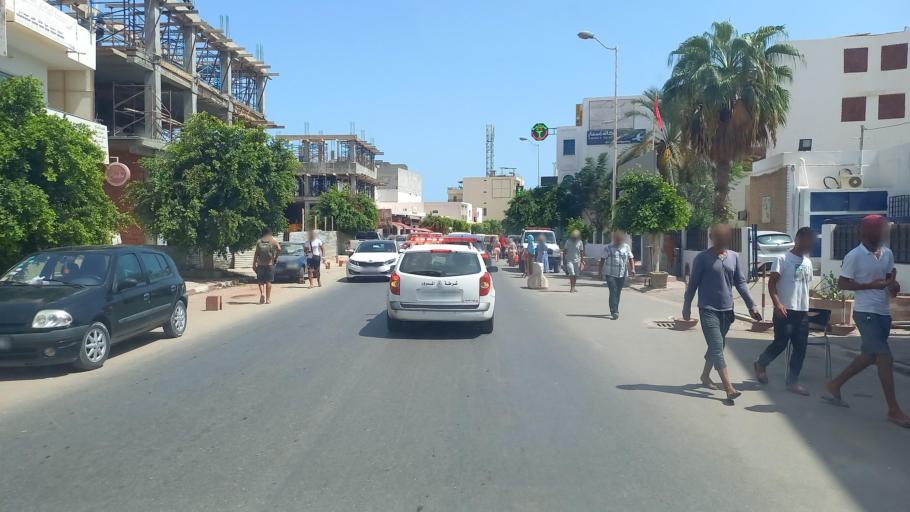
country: TN
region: Madanin
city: Zarzis
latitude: 33.5025
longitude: 11.1070
